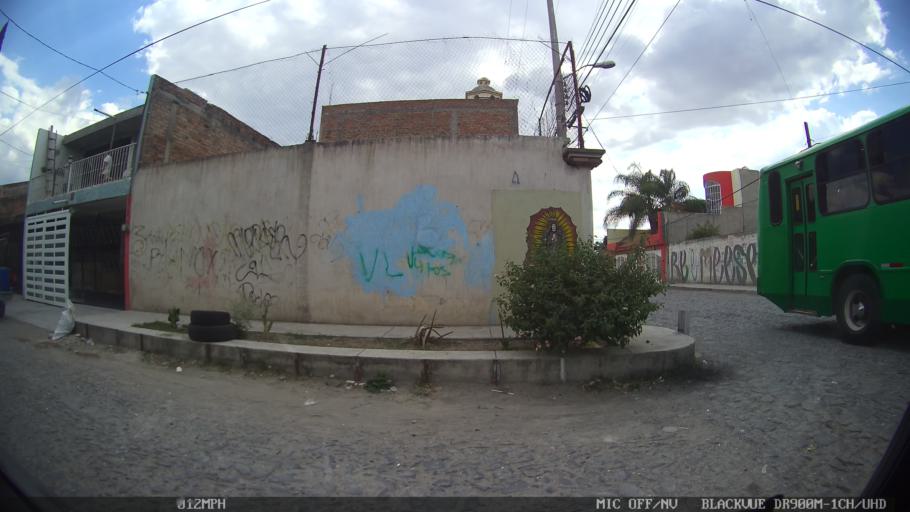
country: MX
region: Jalisco
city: Tlaquepaque
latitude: 20.6553
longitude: -103.2614
